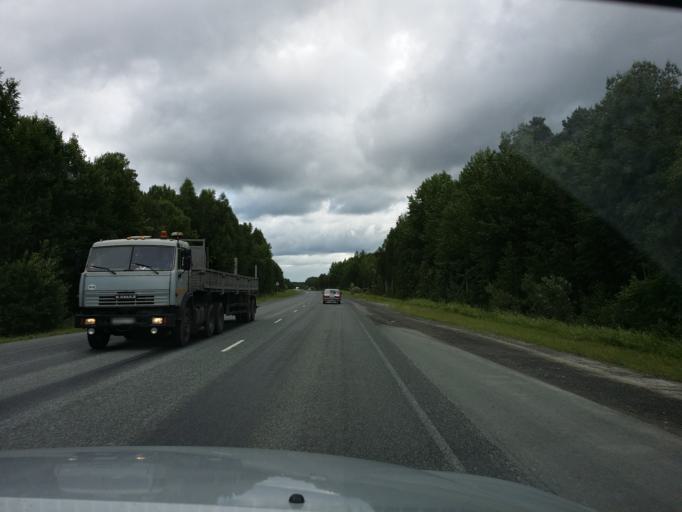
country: RU
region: Tjumen
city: Yarkovo
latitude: 57.6041
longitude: 67.2807
